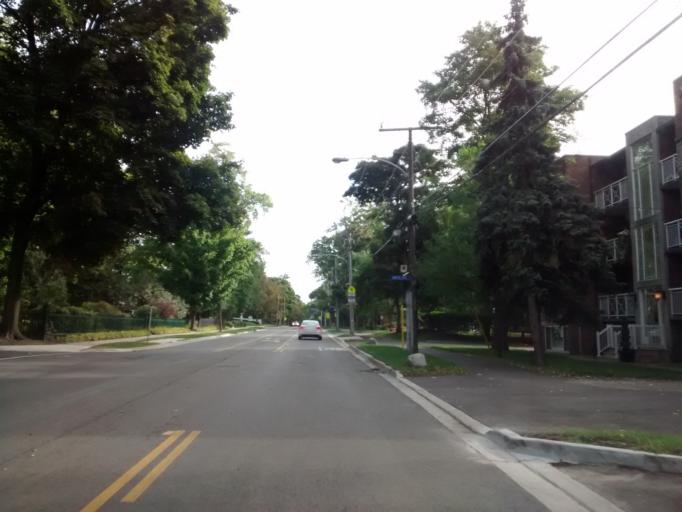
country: CA
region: Ontario
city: Burlington
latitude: 43.3282
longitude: -79.7886
